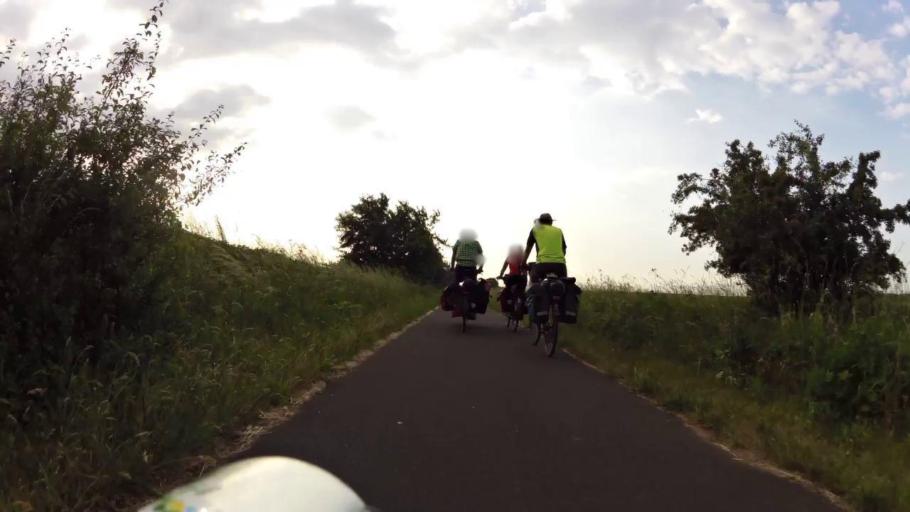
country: PL
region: Kujawsko-Pomorskie
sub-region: Powiat torunski
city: Lubianka
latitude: 53.1536
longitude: 18.4507
